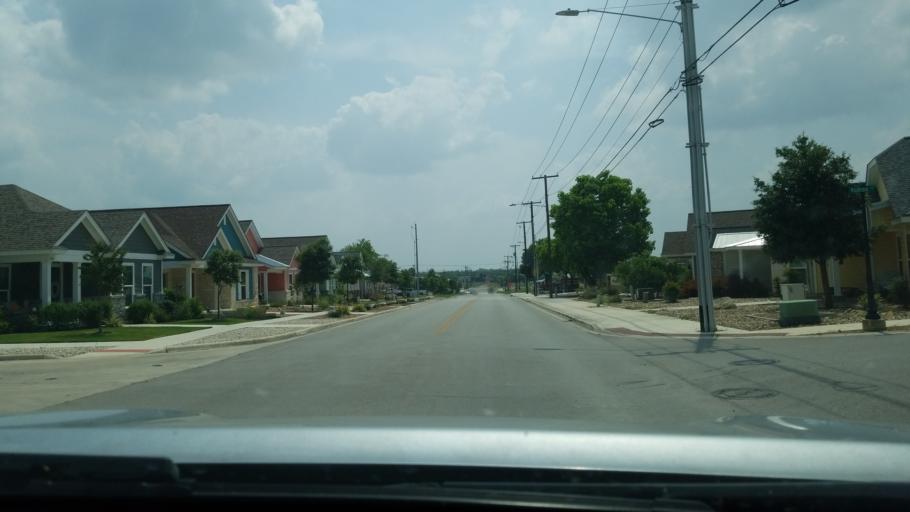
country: US
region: Texas
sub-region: Comal County
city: New Braunfels
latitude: 29.7264
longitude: -98.1056
